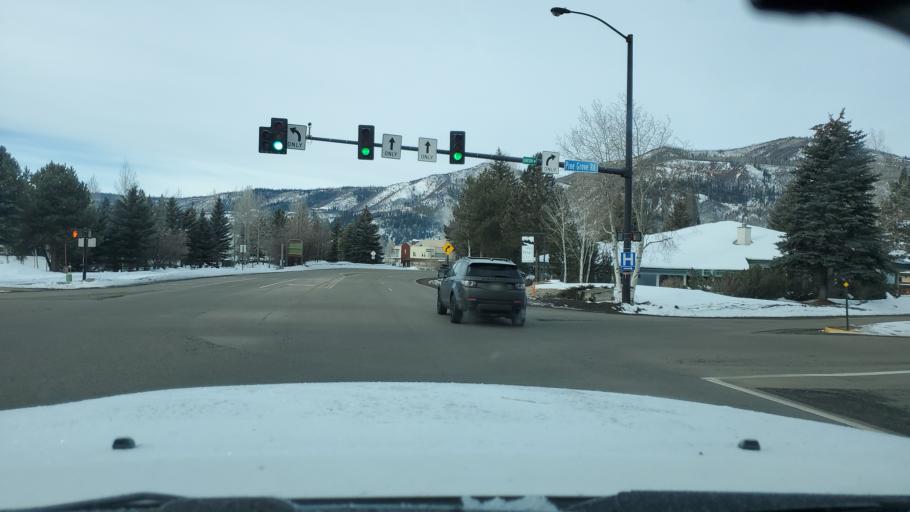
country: US
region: Colorado
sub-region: Routt County
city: Steamboat Springs
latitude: 40.4588
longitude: -106.8160
